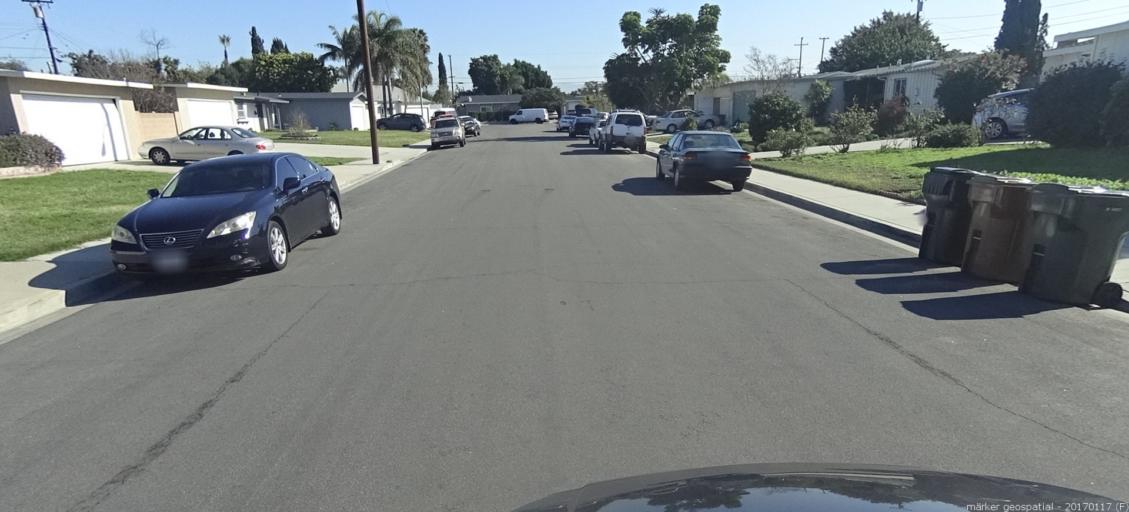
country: US
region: California
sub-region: Orange County
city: Stanton
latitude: 33.8152
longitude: -117.9648
